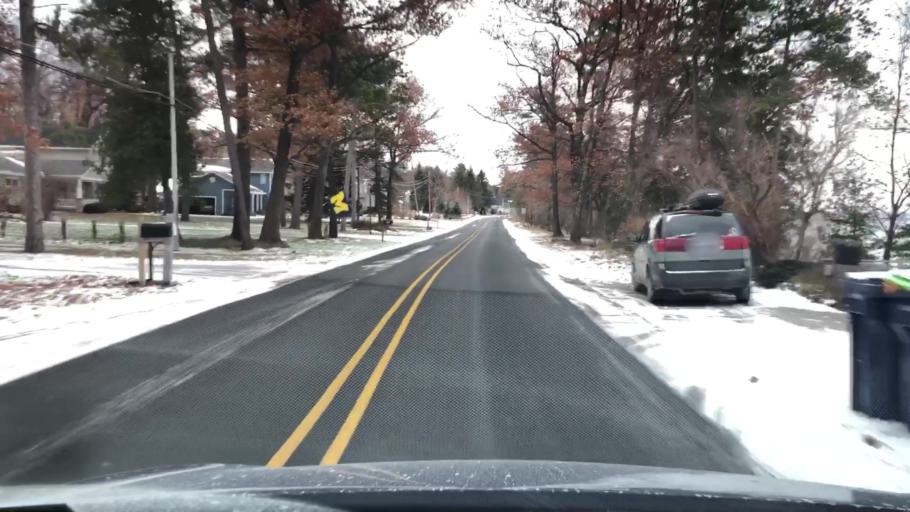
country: US
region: Michigan
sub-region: Grand Traverse County
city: Traverse City
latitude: 44.8147
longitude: -85.5782
